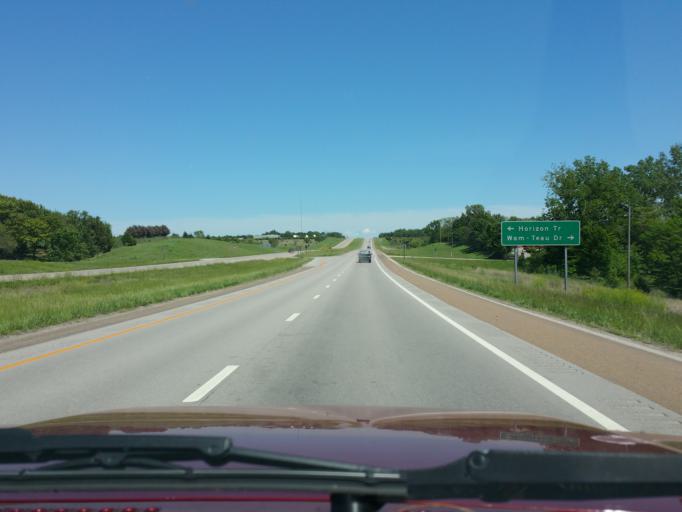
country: US
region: Kansas
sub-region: Pottawatomie County
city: Wamego
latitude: 39.2103
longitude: -96.3654
